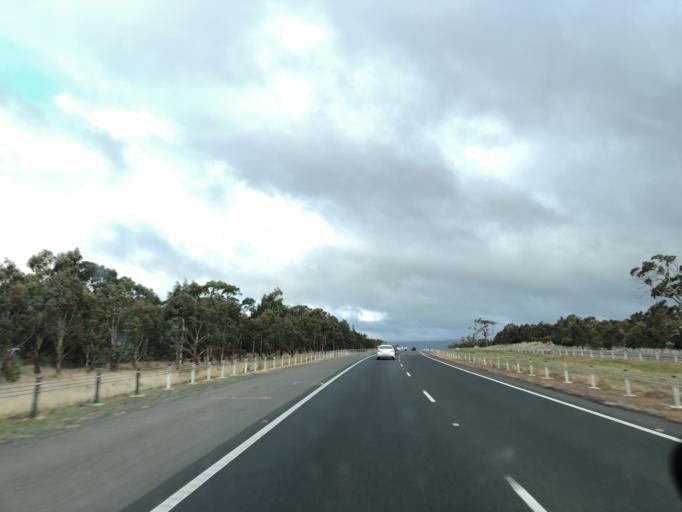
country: AU
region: Victoria
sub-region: Mount Alexander
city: Castlemaine
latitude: -37.2743
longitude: 144.4836
